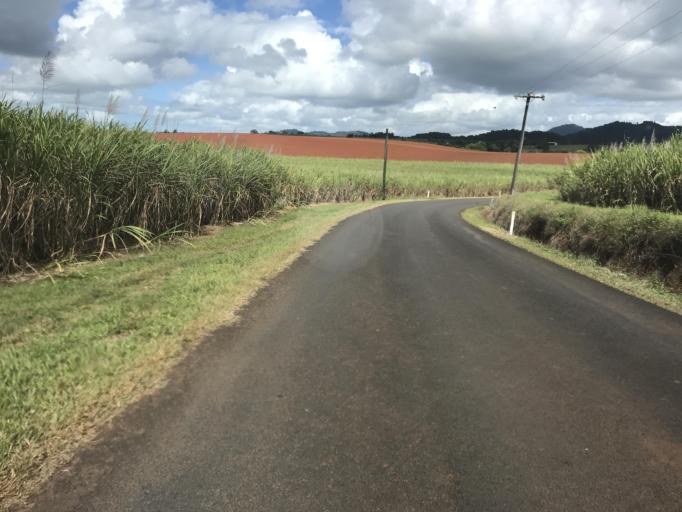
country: AU
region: Queensland
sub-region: Cassowary Coast
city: Innisfail
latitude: -17.5551
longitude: 145.8921
